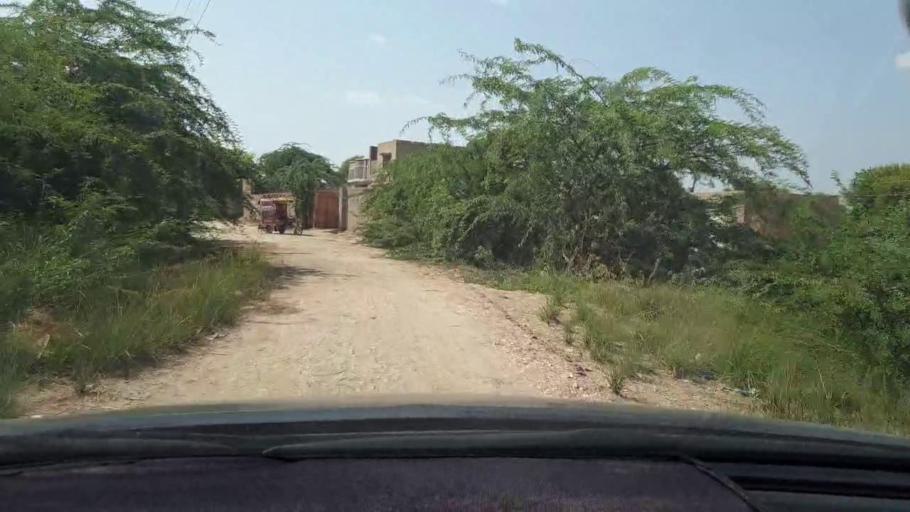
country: PK
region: Sindh
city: Naukot
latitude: 24.9120
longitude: 69.2579
